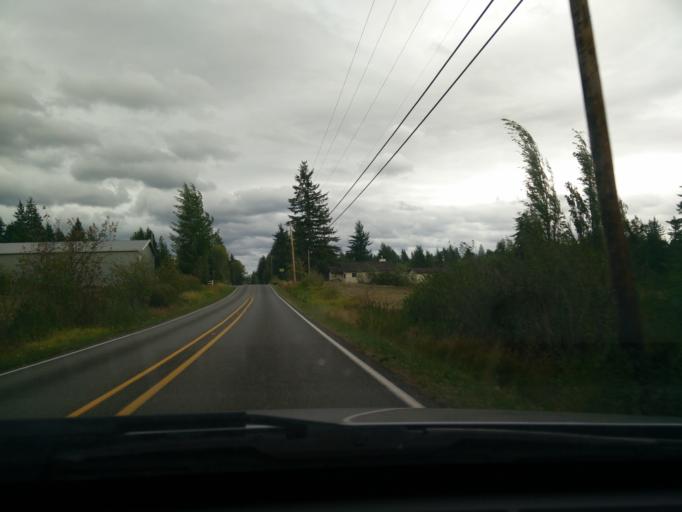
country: US
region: Washington
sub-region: Snohomish County
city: Stanwood
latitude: 48.2681
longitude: -122.2937
